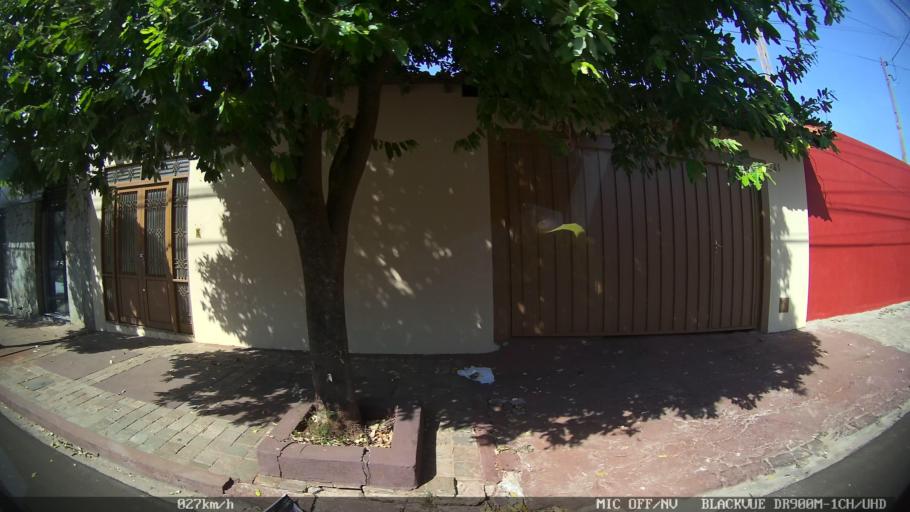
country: BR
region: Sao Paulo
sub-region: Ribeirao Preto
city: Ribeirao Preto
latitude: -21.1844
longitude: -47.8236
